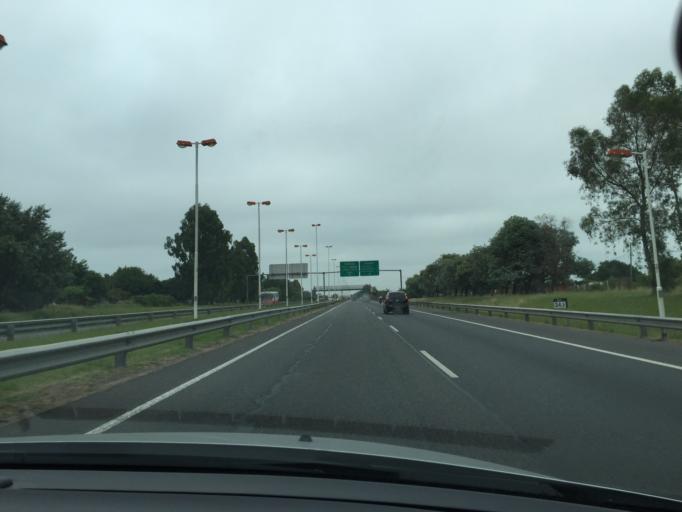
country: AR
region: Buenos Aires
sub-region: Partido de Ezeiza
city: Ezeiza
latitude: -34.8405
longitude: -58.5257
